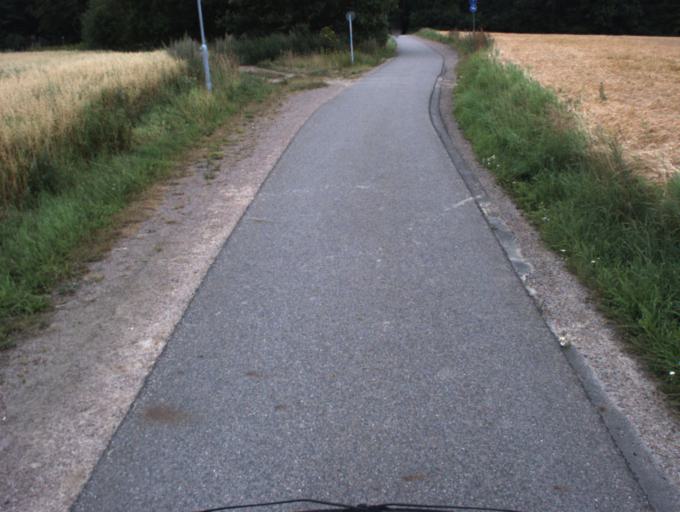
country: SE
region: Skane
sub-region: Helsingborg
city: Helsingborg
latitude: 56.0885
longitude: 12.6662
